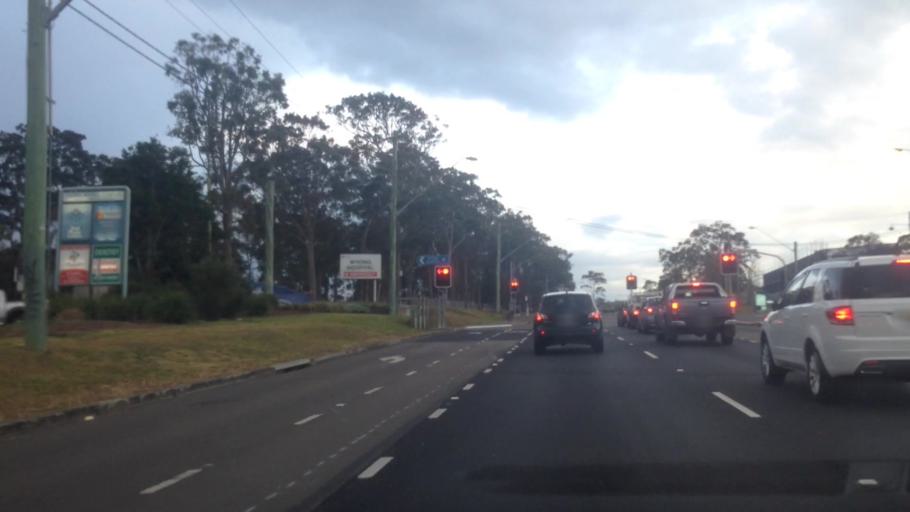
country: AU
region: New South Wales
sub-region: Wyong Shire
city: Kanwal
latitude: -33.2628
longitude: 151.4808
